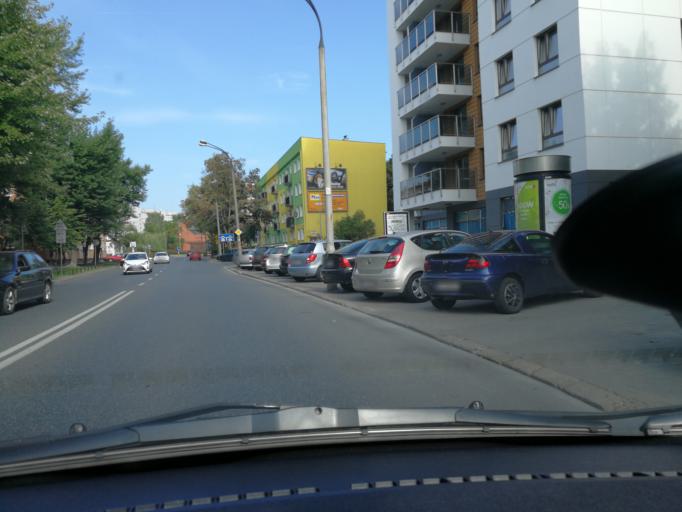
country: PL
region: Masovian Voivodeship
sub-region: Warszawa
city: Bemowo
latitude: 52.2348
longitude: 20.9405
